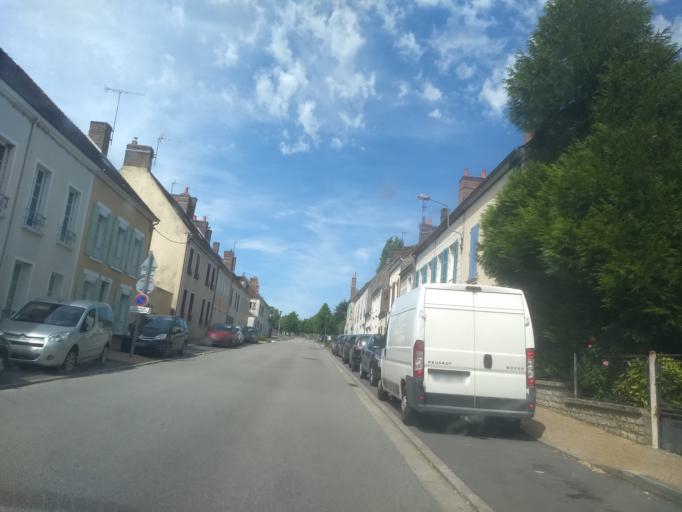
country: FR
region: Lower Normandy
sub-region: Departement de l'Orne
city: Remalard
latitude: 48.4307
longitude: 0.7743
